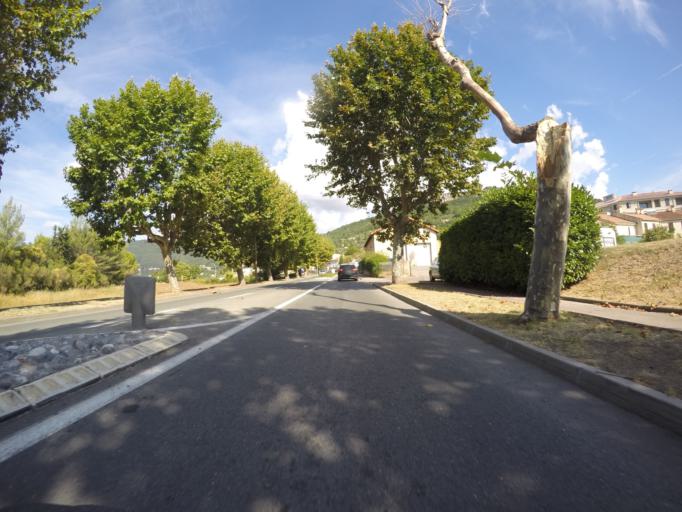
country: FR
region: Provence-Alpes-Cote d'Azur
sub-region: Departement des Alpes-Maritimes
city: Opio
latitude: 43.6796
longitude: 6.9726
